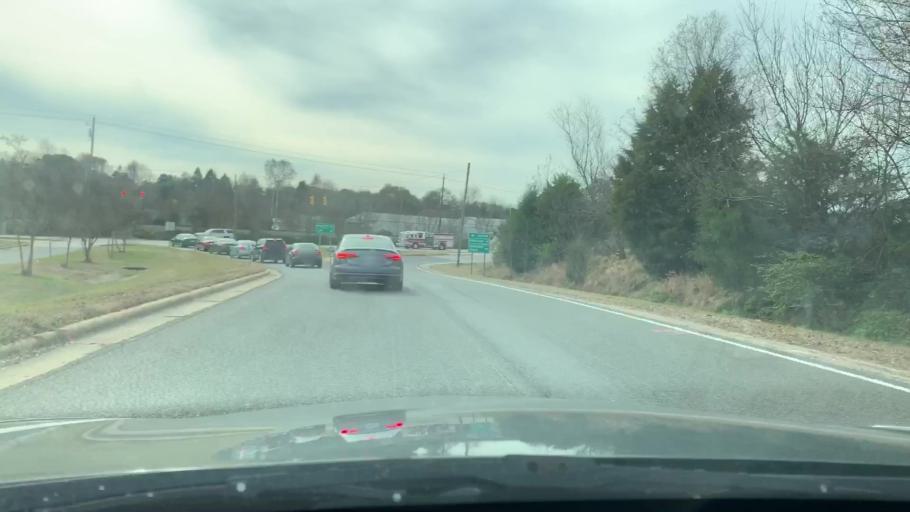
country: US
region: North Carolina
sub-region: Wake County
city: West Raleigh
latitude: 35.7965
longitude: -78.6960
